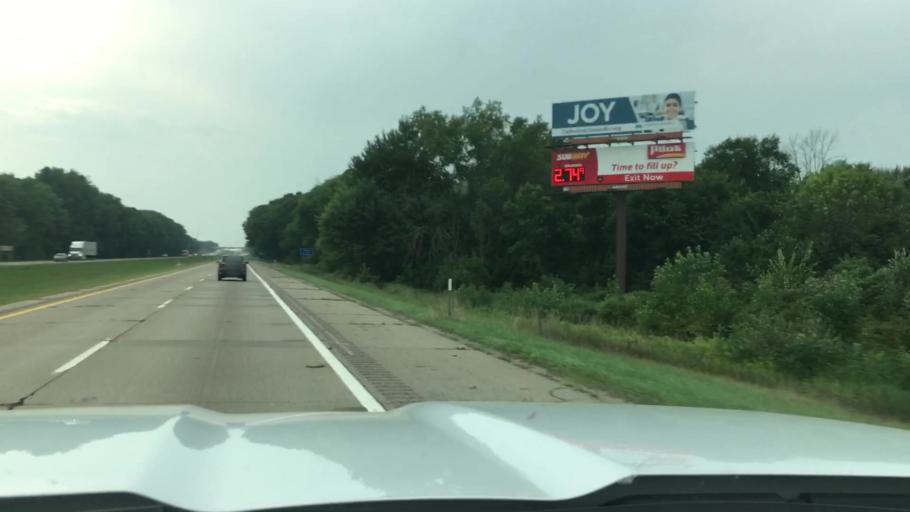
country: US
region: Michigan
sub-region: Ionia County
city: Ionia
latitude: 42.8799
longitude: -85.0545
